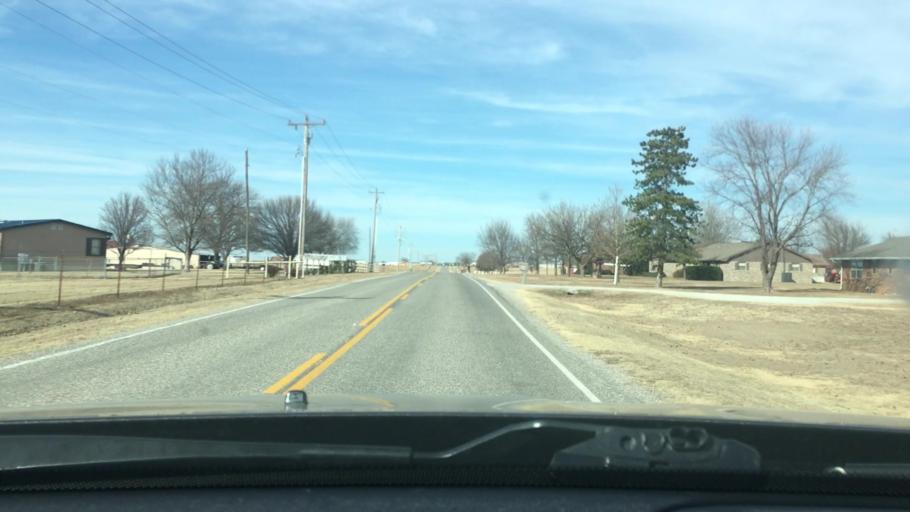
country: US
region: Oklahoma
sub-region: Murray County
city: Davis
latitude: 34.4966
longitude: -97.0904
